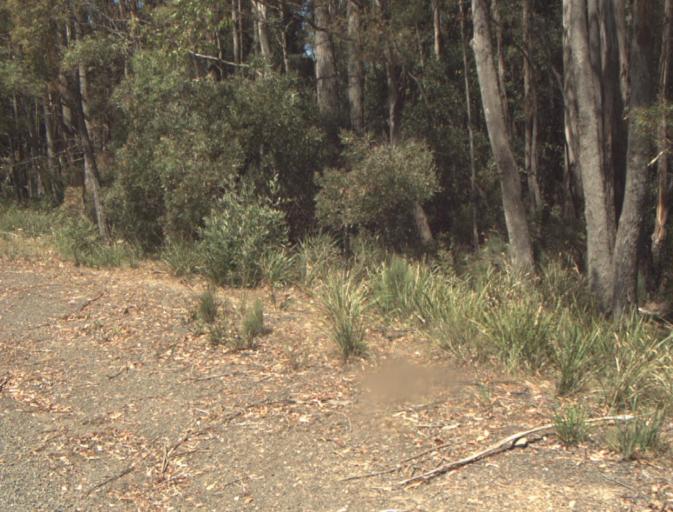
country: AU
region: Tasmania
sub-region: Launceston
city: Newstead
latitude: -41.3452
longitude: 147.3711
